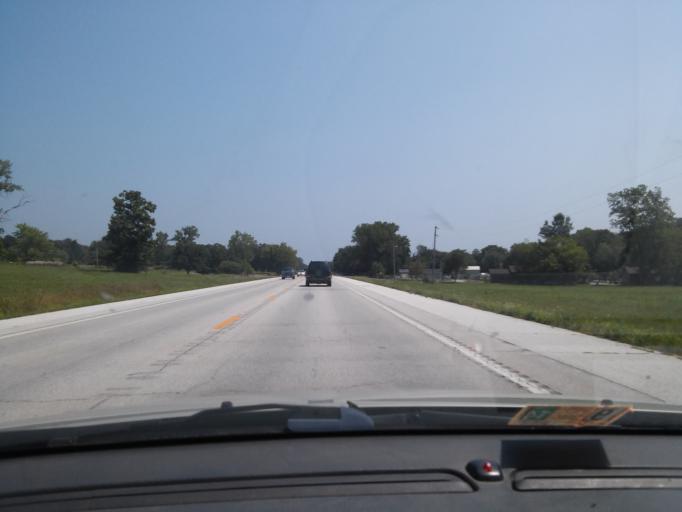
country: US
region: Missouri
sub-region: Pike County
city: Bowling Green
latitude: 39.3725
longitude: -91.1659
